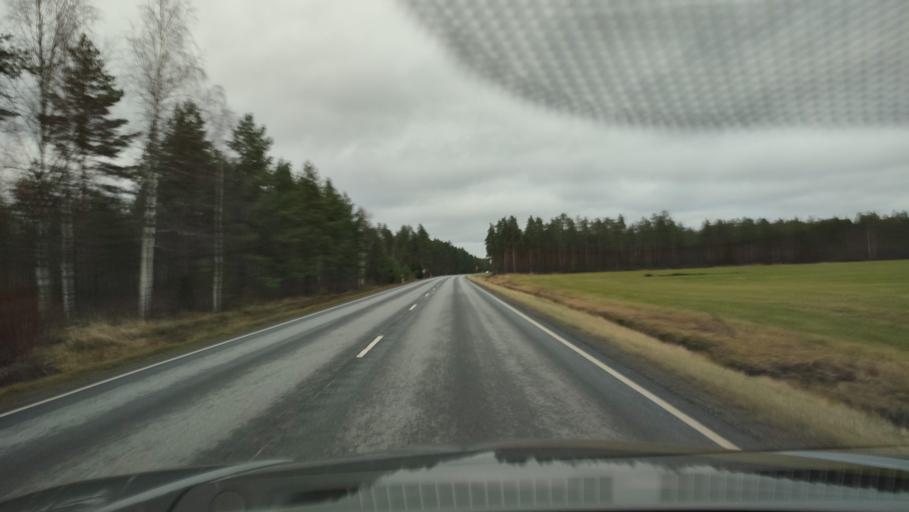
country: FI
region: Southern Ostrobothnia
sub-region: Seinaejoki
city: Kurikka
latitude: 62.5137
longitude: 22.3118
